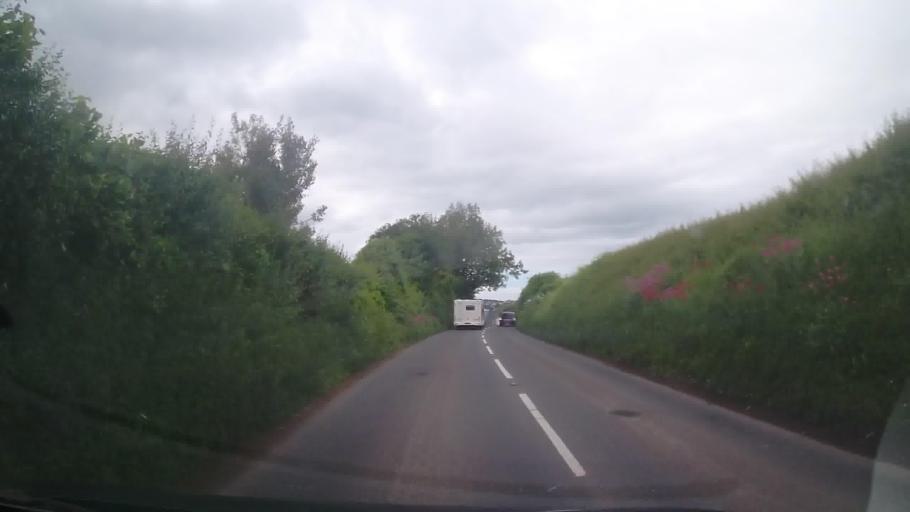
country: GB
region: England
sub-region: Devon
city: Kingsbridge
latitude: 50.2696
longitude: -3.7577
